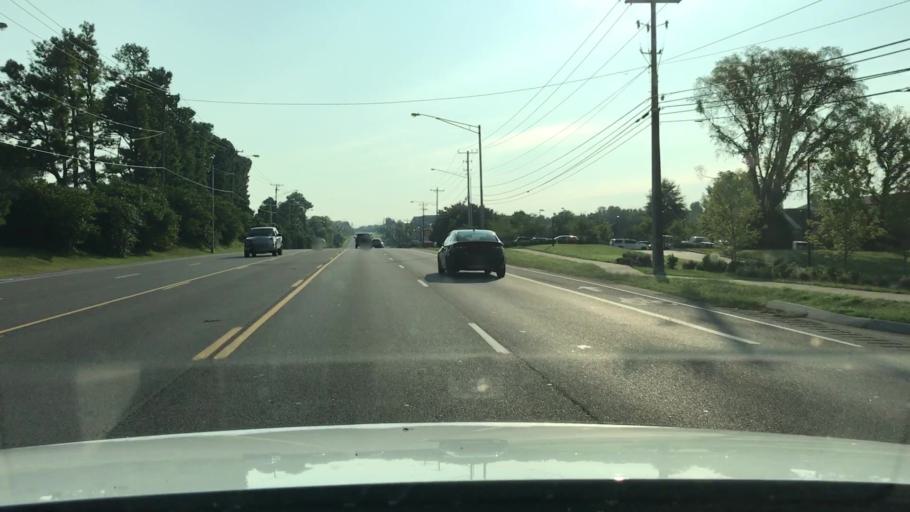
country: US
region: Tennessee
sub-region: Sumner County
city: Hendersonville
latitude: 36.3198
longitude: -86.5784
